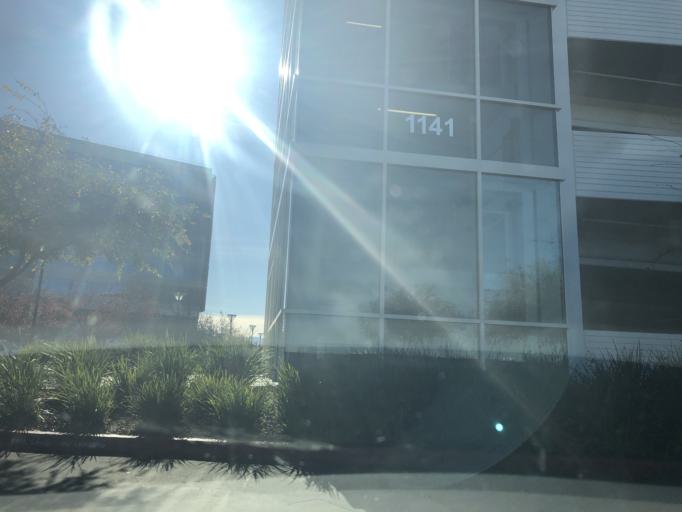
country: US
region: California
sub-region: Santa Clara County
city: Sunnyvale
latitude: 37.4095
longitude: -122.0295
